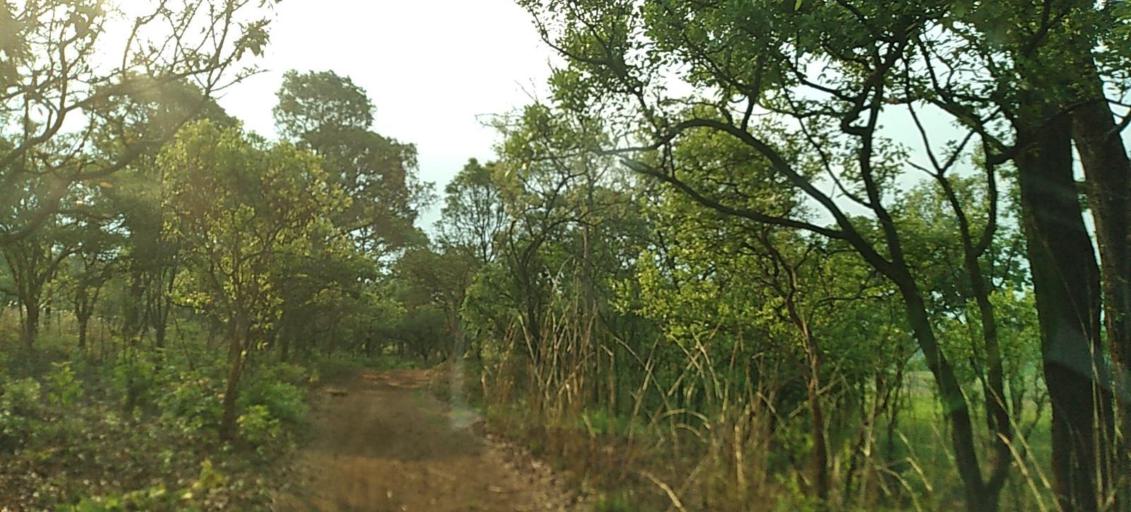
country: ZM
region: North-Western
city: Solwezi
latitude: -12.0439
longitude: 26.0534
